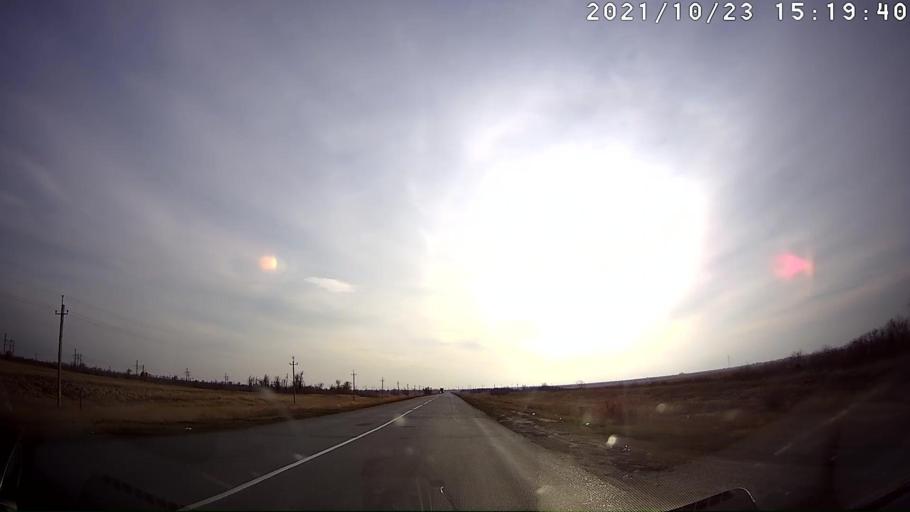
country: RU
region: Volgograd
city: Bereslavka
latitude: 48.3273
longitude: 44.3314
